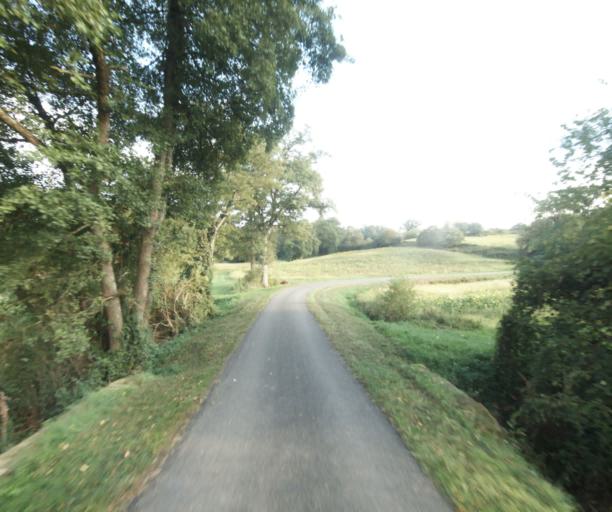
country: FR
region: Midi-Pyrenees
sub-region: Departement du Gers
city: Le Houga
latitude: 43.8455
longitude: -0.1239
